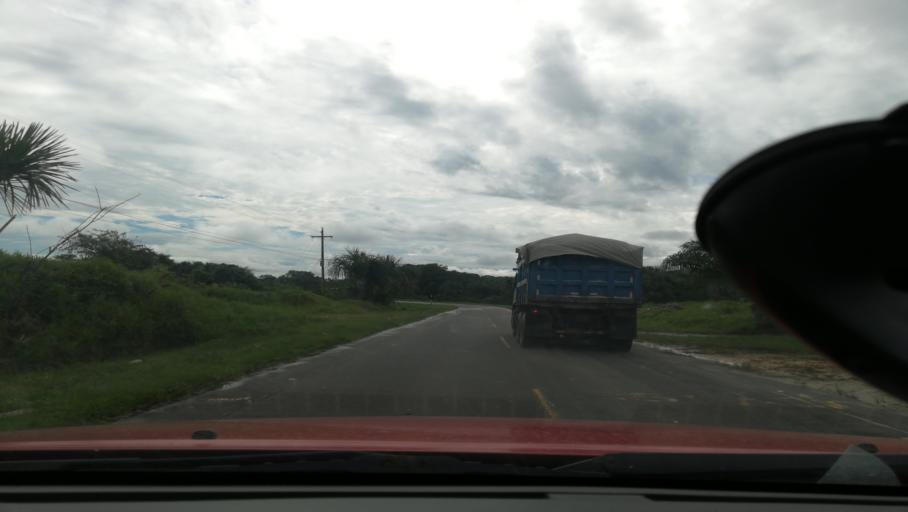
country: PE
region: Loreto
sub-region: Provincia de Maynas
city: San Juan
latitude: -3.9225
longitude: -73.3720
